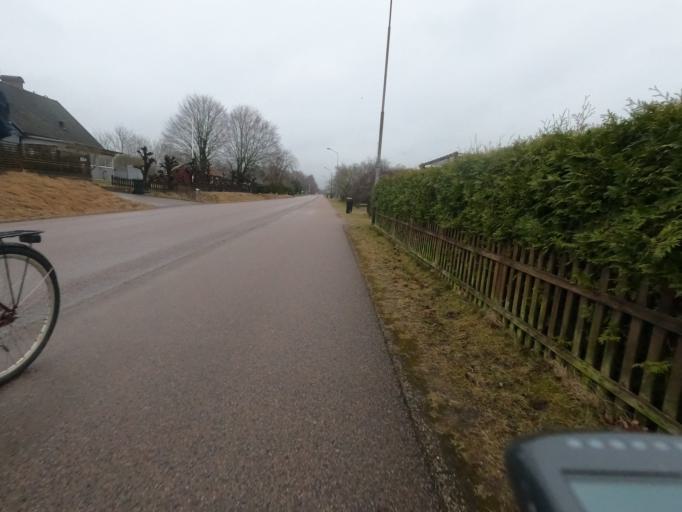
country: SE
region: Halland
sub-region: Halmstads Kommun
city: Fyllinge
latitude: 56.6797
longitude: 12.9322
